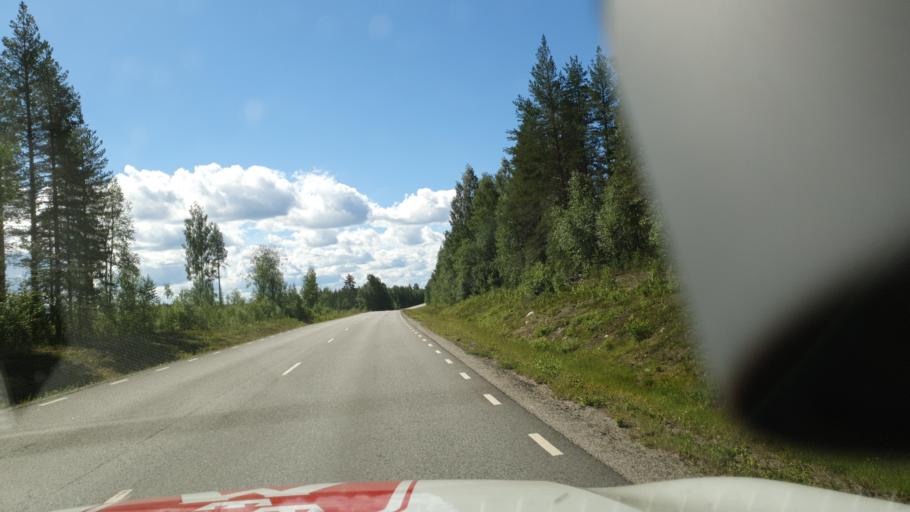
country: SE
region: Vaesterbotten
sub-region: Lycksele Kommun
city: Lycksele
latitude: 64.6857
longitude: 18.6989
